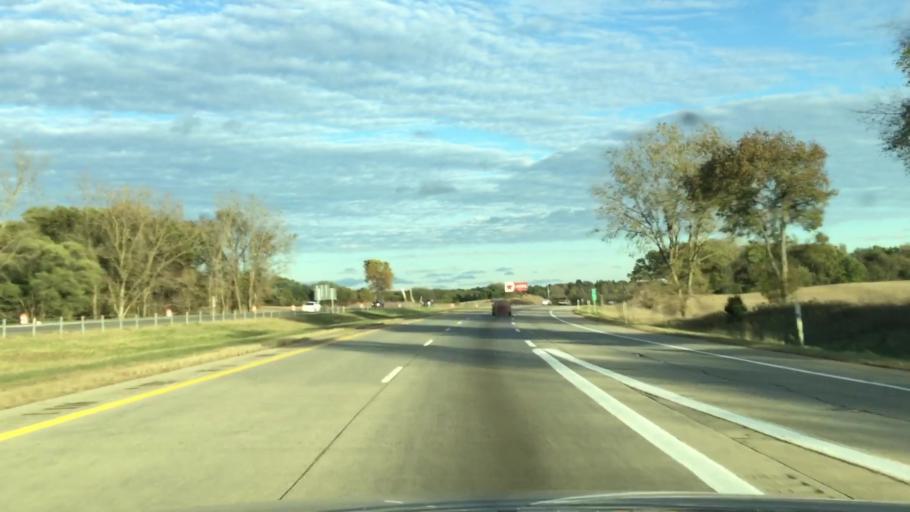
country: US
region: Michigan
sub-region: Calhoun County
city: Albion
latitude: 42.2835
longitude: -84.7981
